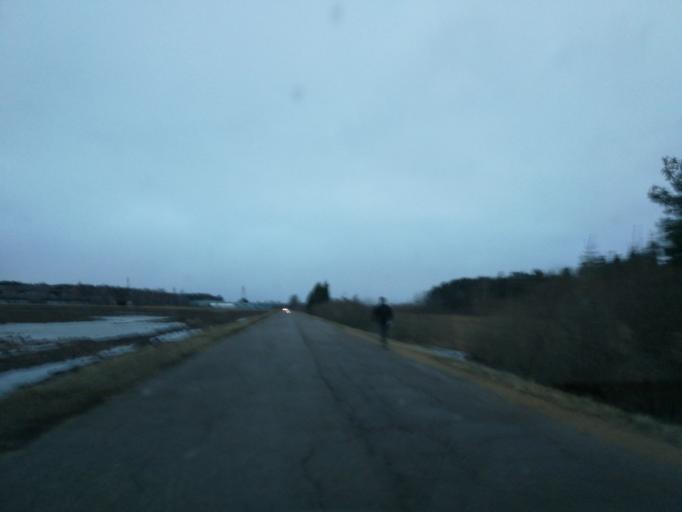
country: LV
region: Adazi
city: Adazi
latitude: 57.0779
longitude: 24.2849
